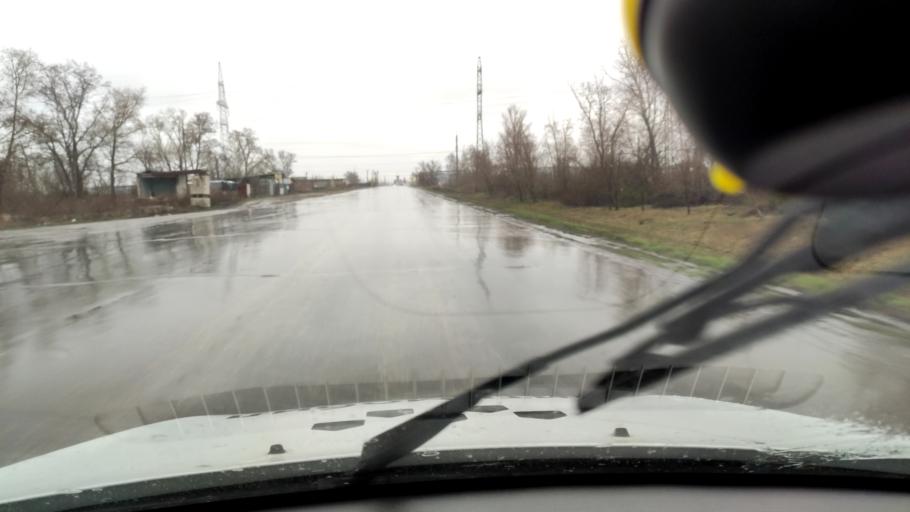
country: RU
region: Samara
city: Tol'yatti
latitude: 53.5837
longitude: 49.4042
